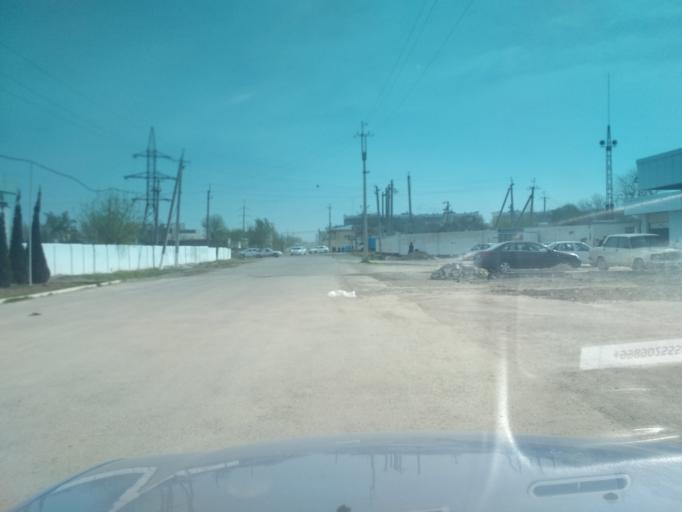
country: UZ
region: Sirdaryo
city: Guliston
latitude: 40.5034
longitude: 68.7673
